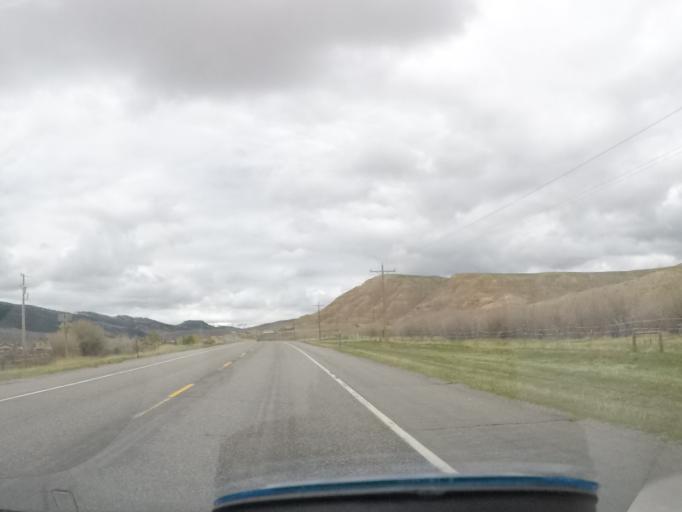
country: US
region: Wyoming
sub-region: Sublette County
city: Pinedale
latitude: 43.5667
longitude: -109.7072
